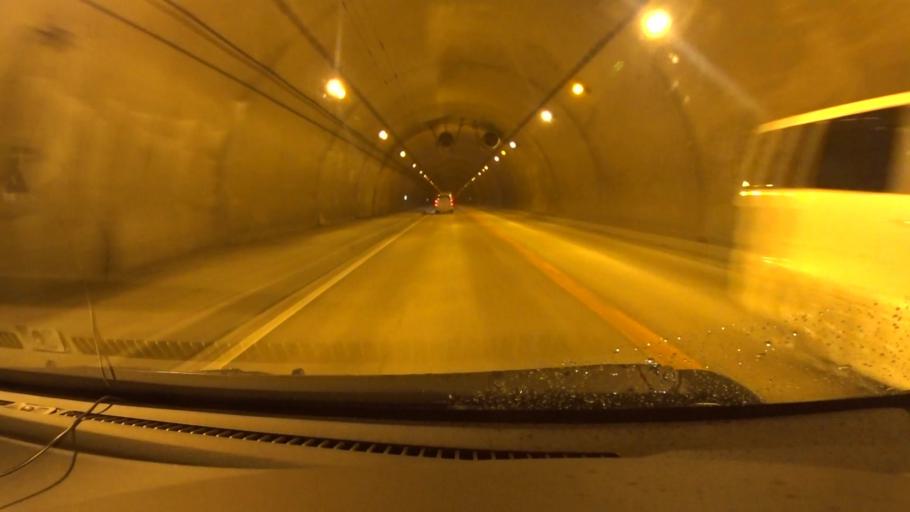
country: JP
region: Kyoto
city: Ayabe
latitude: 35.2670
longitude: 135.4021
